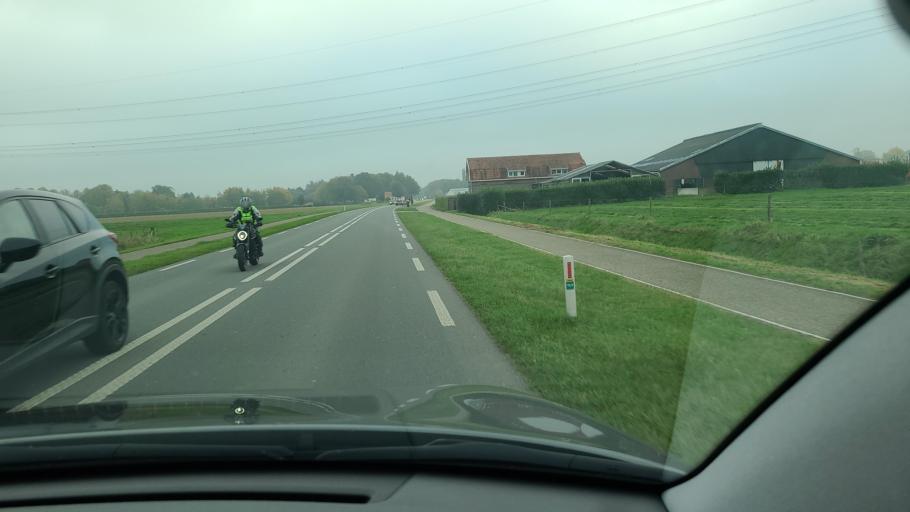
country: NL
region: North Brabant
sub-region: Gemeente Grave
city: Grave
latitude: 51.7594
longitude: 5.8001
